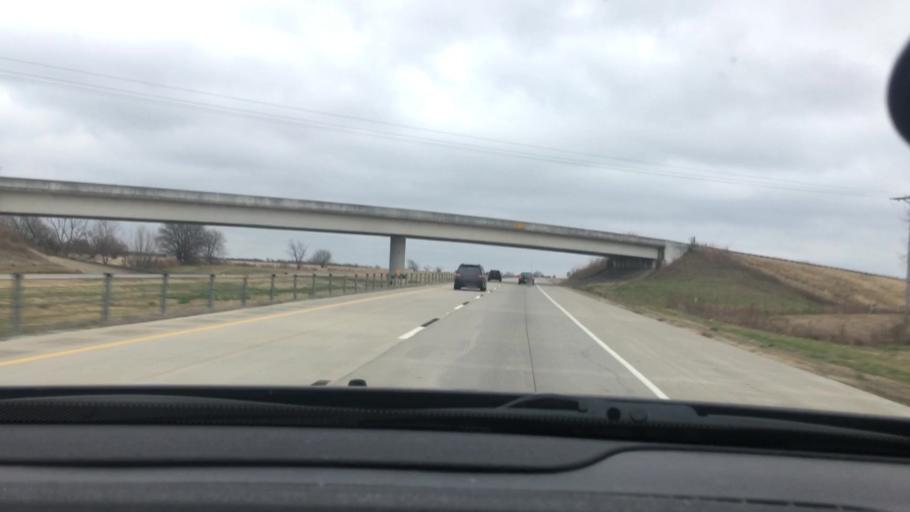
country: US
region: Oklahoma
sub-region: Bryan County
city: Durant
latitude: 34.1128
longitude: -96.2993
